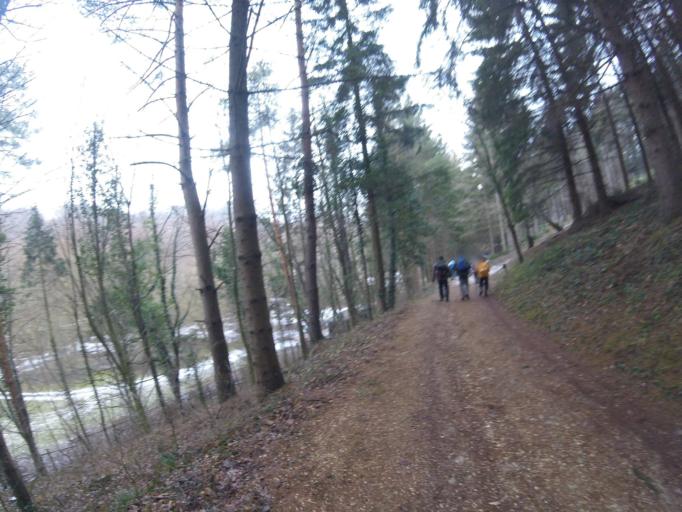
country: HU
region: Pest
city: Visegrad
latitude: 47.7692
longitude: 18.9835
